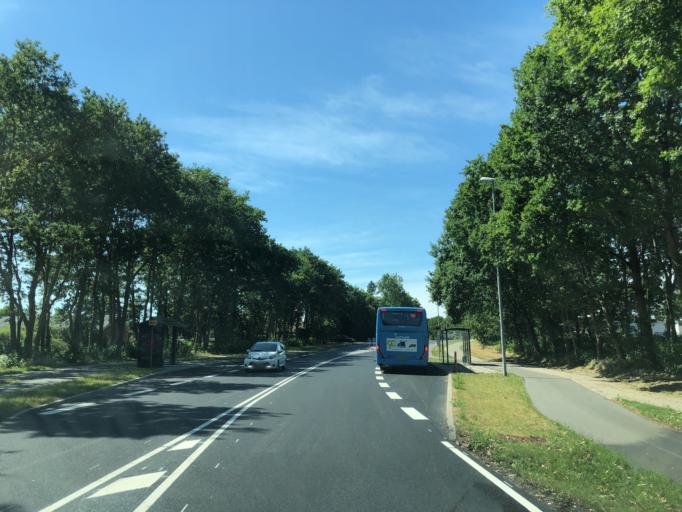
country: DK
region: Central Jutland
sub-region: Skive Kommune
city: Skive
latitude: 56.5537
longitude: 9.0211
